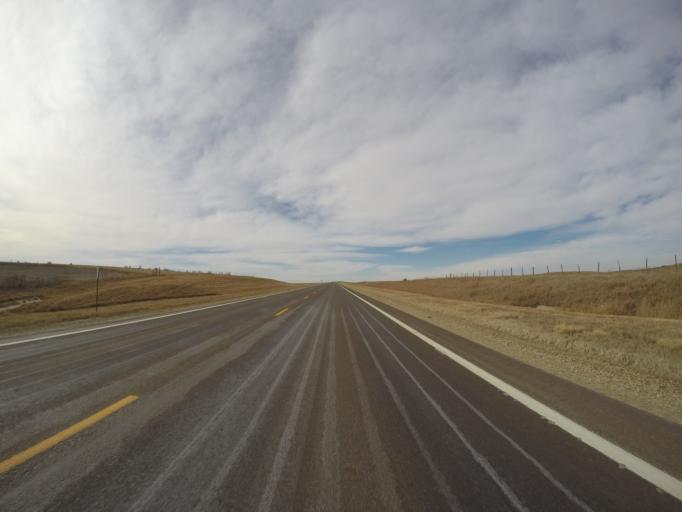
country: US
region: Kansas
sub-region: Washington County
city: Washington
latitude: 39.8157
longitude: -96.9321
